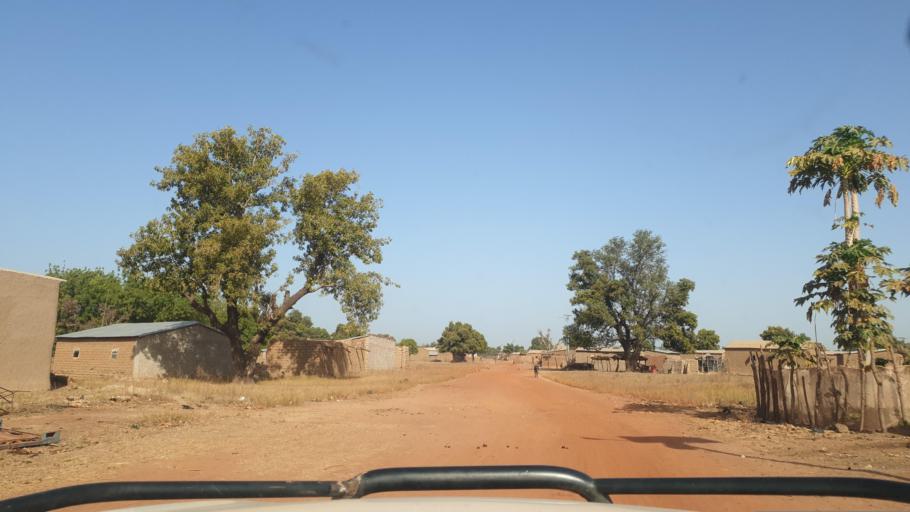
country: ML
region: Sikasso
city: Kolondieba
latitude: 11.7301
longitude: -6.8892
